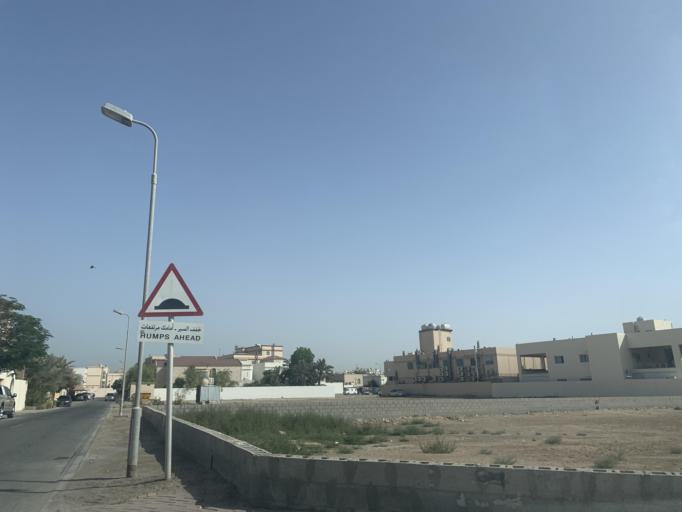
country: BH
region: Northern
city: Madinat `Isa
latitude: 26.1651
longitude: 50.5715
